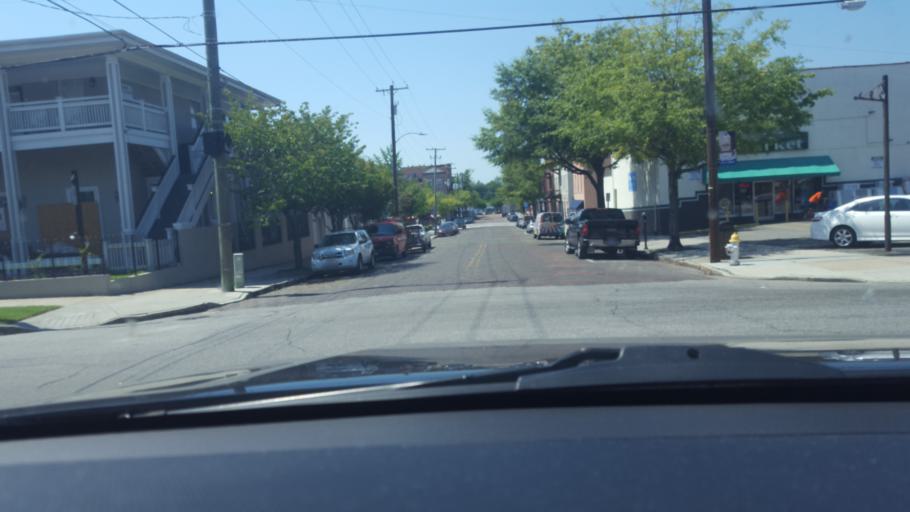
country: US
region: North Carolina
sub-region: New Hanover County
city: Wilmington
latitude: 34.2343
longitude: -77.9472
